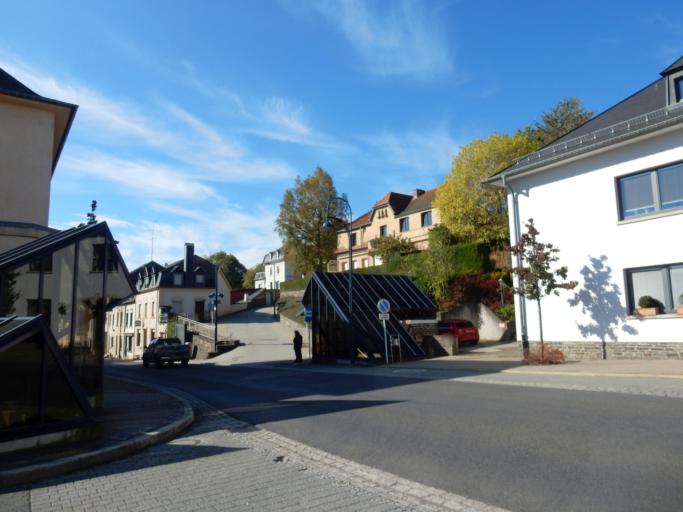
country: LU
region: Diekirch
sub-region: Canton de Clervaux
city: Troisvierges
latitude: 50.1215
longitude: 6.0012
